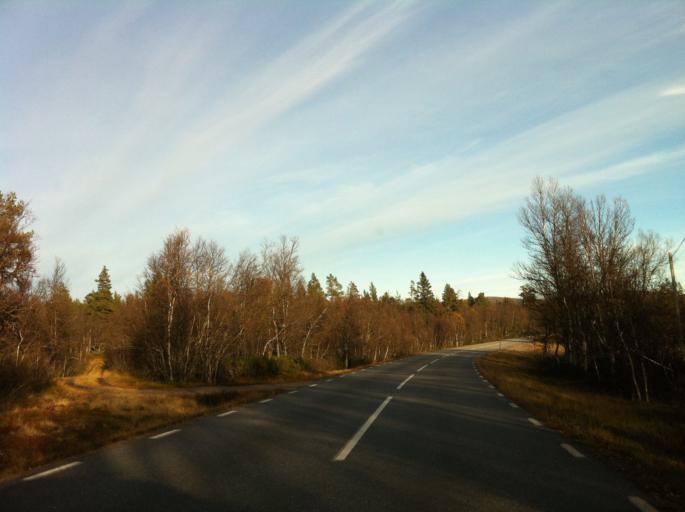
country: NO
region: Hedmark
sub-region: Engerdal
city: Engerdal
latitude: 62.0716
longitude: 12.1966
